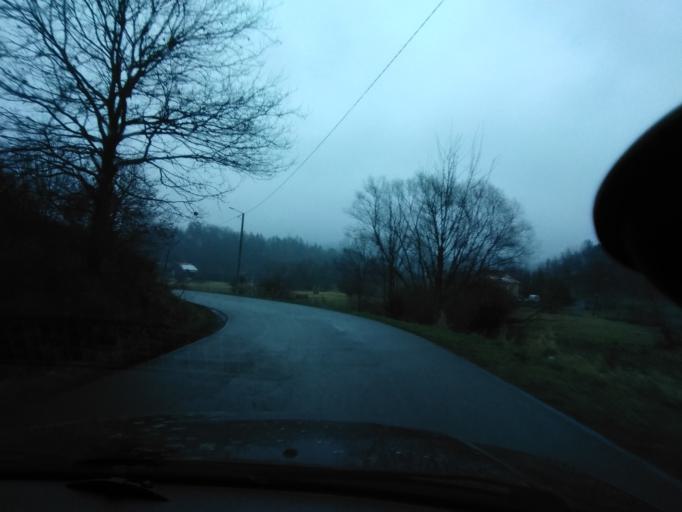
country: PL
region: Subcarpathian Voivodeship
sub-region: Powiat brzozowski
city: Jablonka
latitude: 49.7361
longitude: 22.1437
